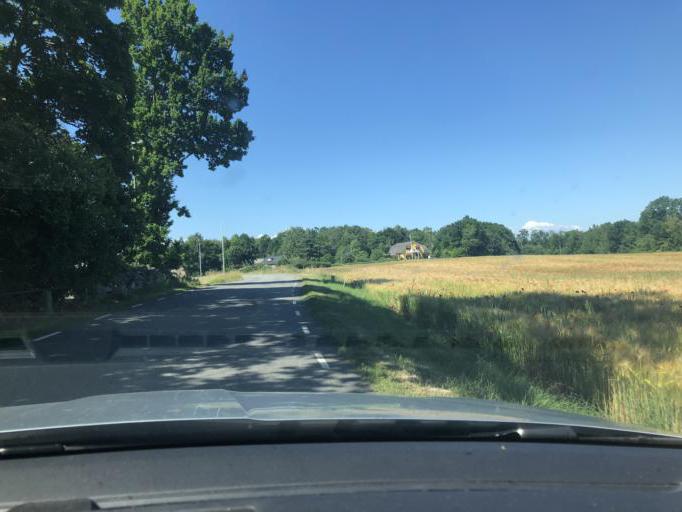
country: SE
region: Blekinge
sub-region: Karlshamns Kommun
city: Morrum
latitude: 56.1684
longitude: 14.6816
